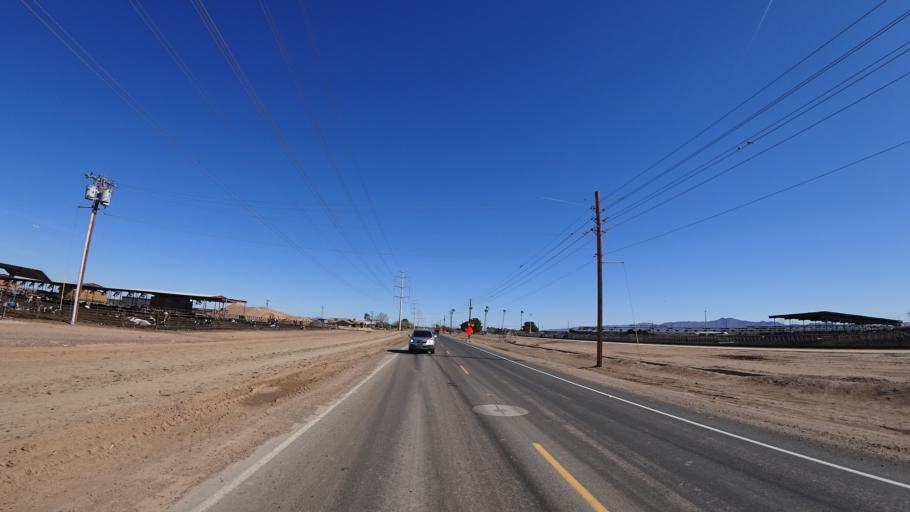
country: US
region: Arizona
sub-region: Maricopa County
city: Tolleson
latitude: 33.4073
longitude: -112.2483
